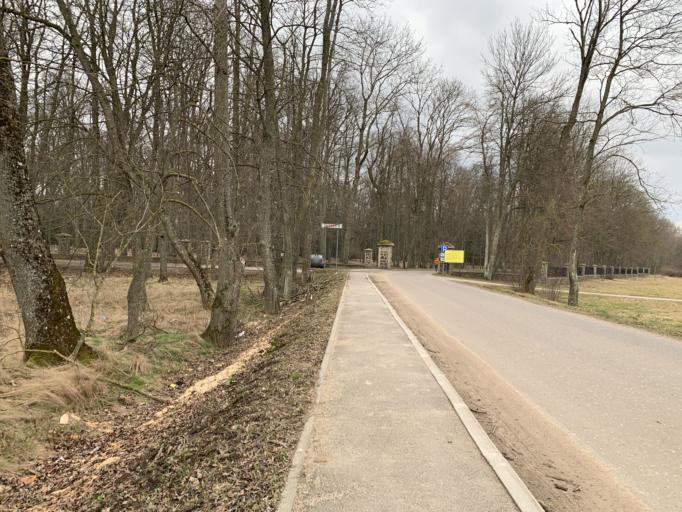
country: BY
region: Minsk
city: Nyasvizh
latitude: 53.2279
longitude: 26.6918
